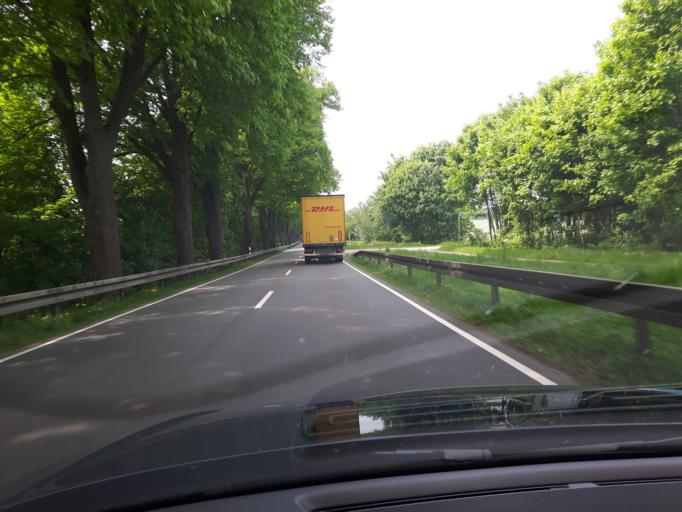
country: DE
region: Mecklenburg-Vorpommern
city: Selmsdorf
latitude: 53.8689
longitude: 10.8964
